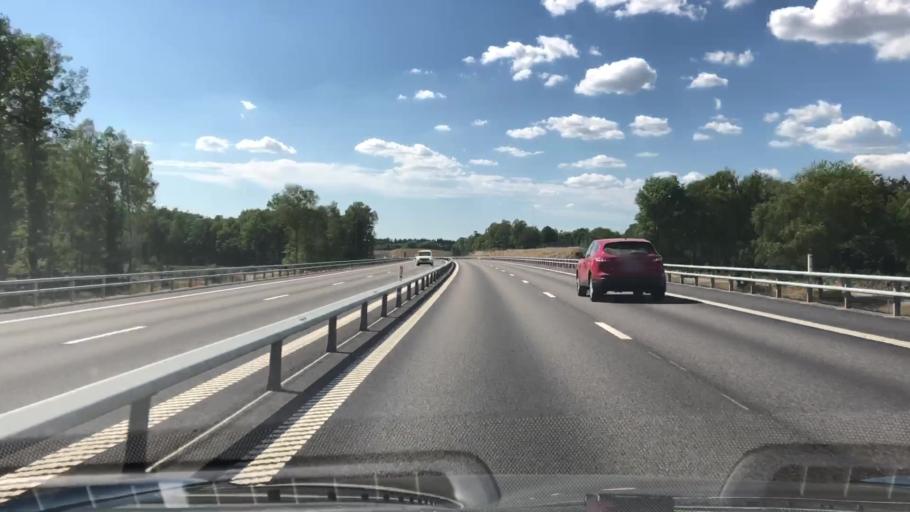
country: SE
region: Skane
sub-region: Horby Kommun
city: Hoerby
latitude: 55.9260
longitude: 13.8141
